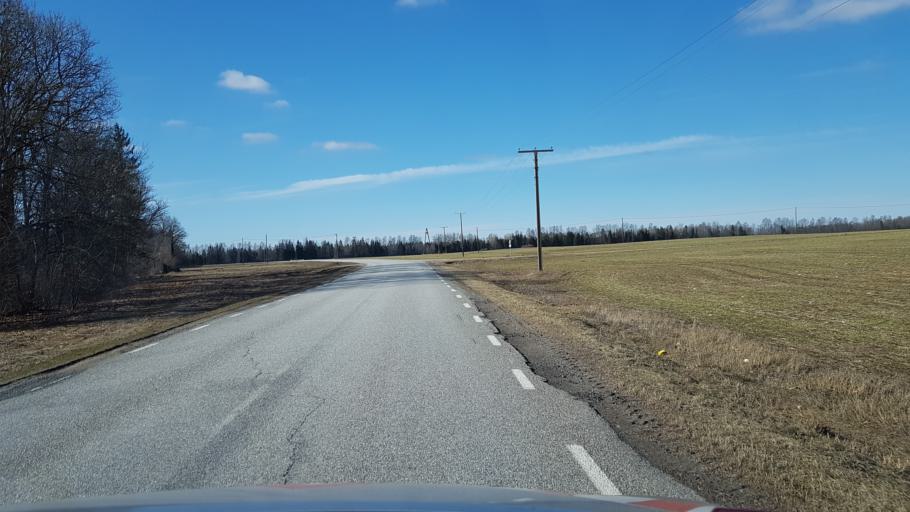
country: EE
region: Laeaene-Virumaa
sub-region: Tapa vald
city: Tapa
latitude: 59.2724
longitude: 26.0060
